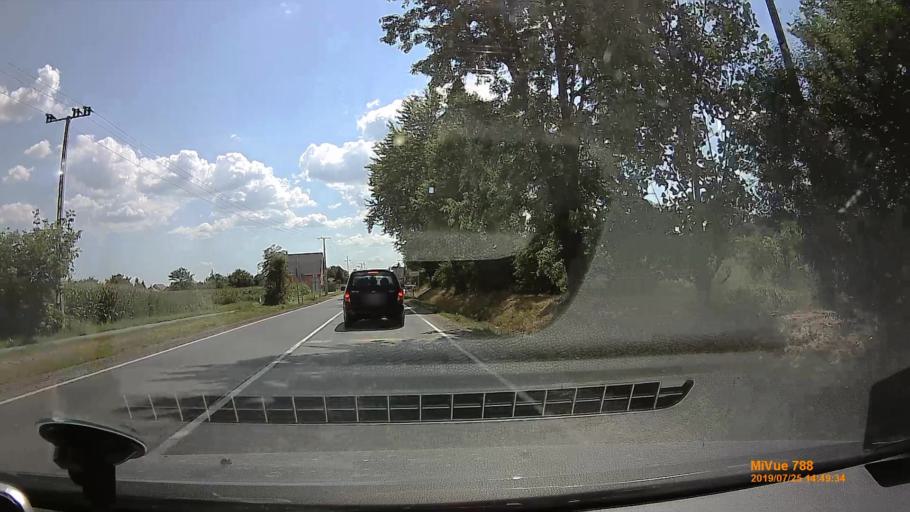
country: HU
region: Borsod-Abauj-Zemplen
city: Aszalo
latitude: 48.2271
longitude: 20.9562
